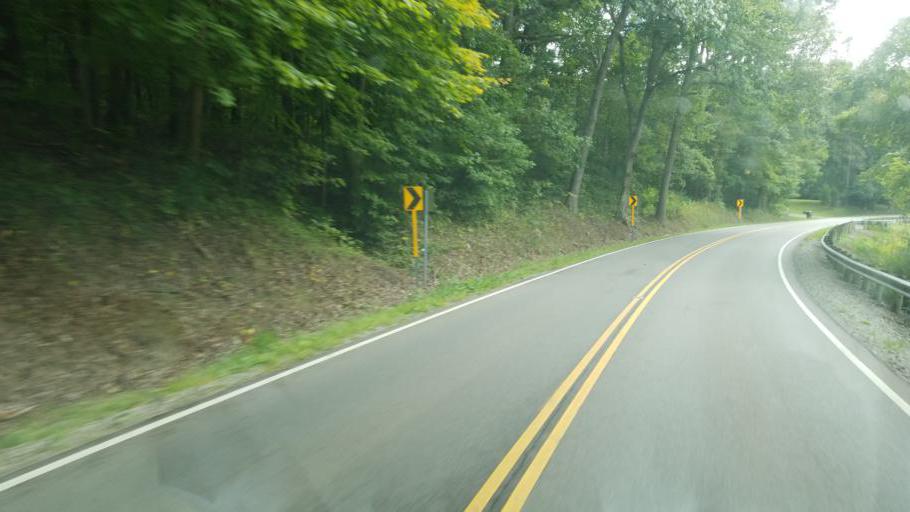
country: US
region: Ohio
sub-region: Jackson County
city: Jackson
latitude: 38.9903
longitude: -82.6585
